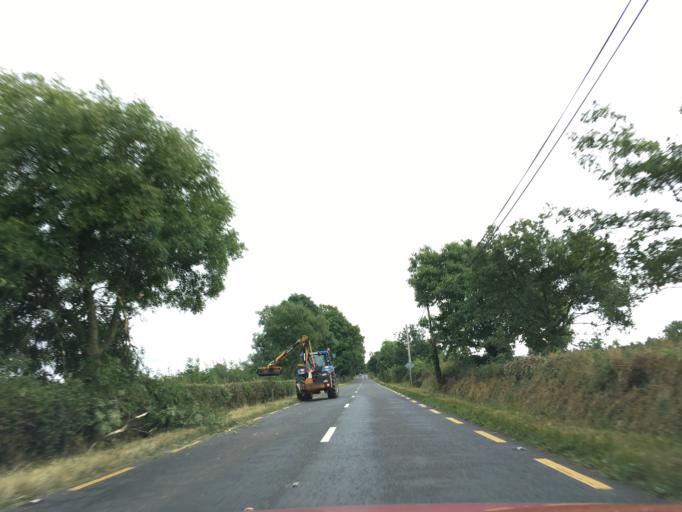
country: IE
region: Munster
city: Fethard
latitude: 52.4350
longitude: -7.7892
